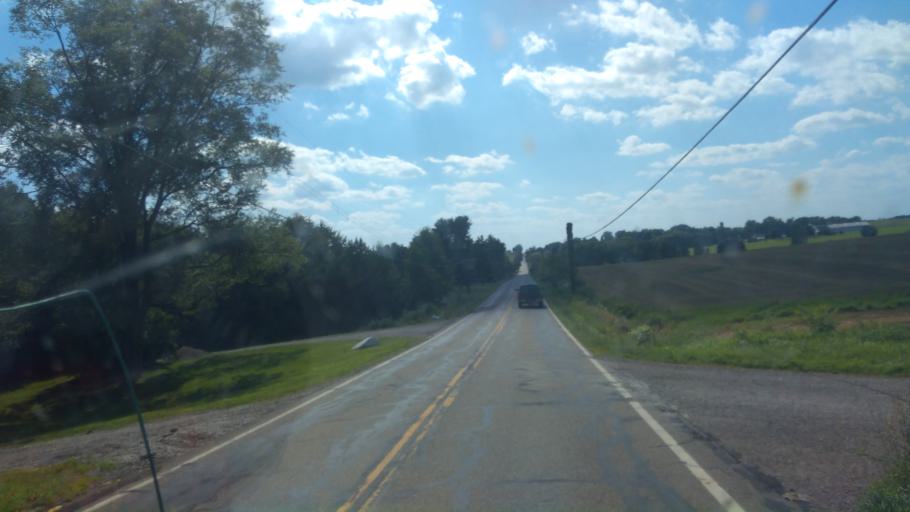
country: US
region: Ohio
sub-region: Stark County
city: Richville
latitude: 40.7298
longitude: -81.4373
